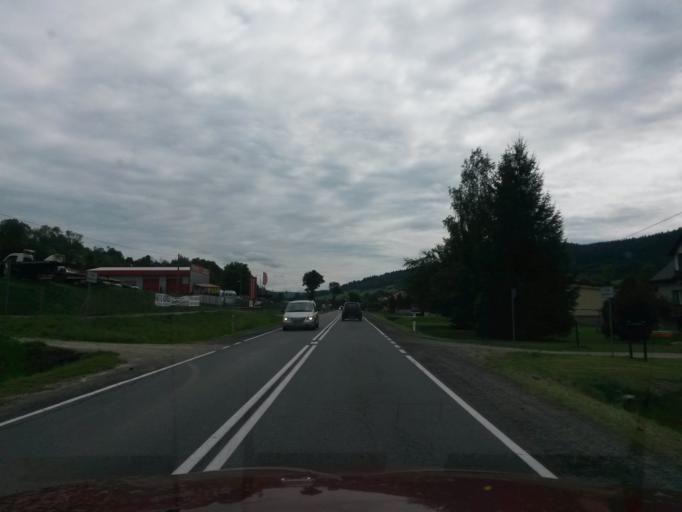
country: PL
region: Lesser Poland Voivodeship
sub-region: Powiat nowosadecki
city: Labowa
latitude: 49.5129
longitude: 20.8848
